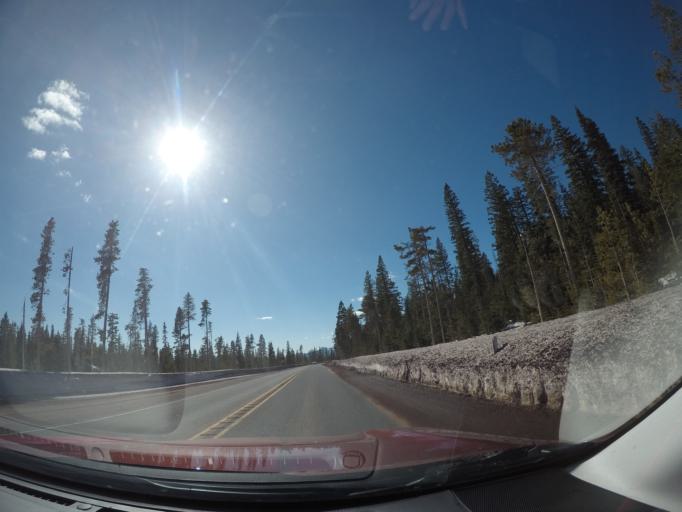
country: US
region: Oregon
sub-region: Deschutes County
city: Sunriver
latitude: 43.9823
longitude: -121.5817
